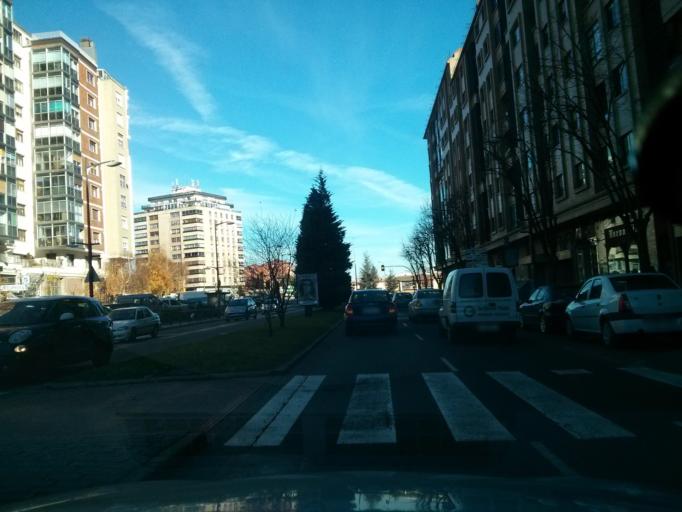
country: ES
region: Castille and Leon
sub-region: Provincia de Burgos
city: Burgos
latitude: 42.3535
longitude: -3.6927
